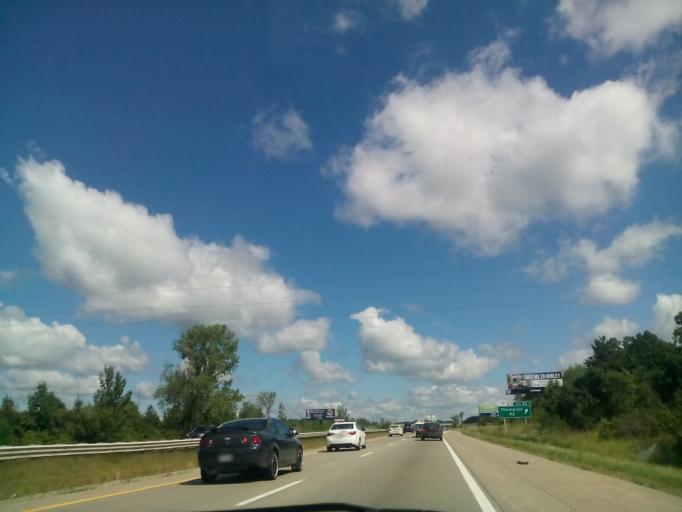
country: US
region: Michigan
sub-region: Genesee County
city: Lake Fenton
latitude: 42.8571
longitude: -83.7396
